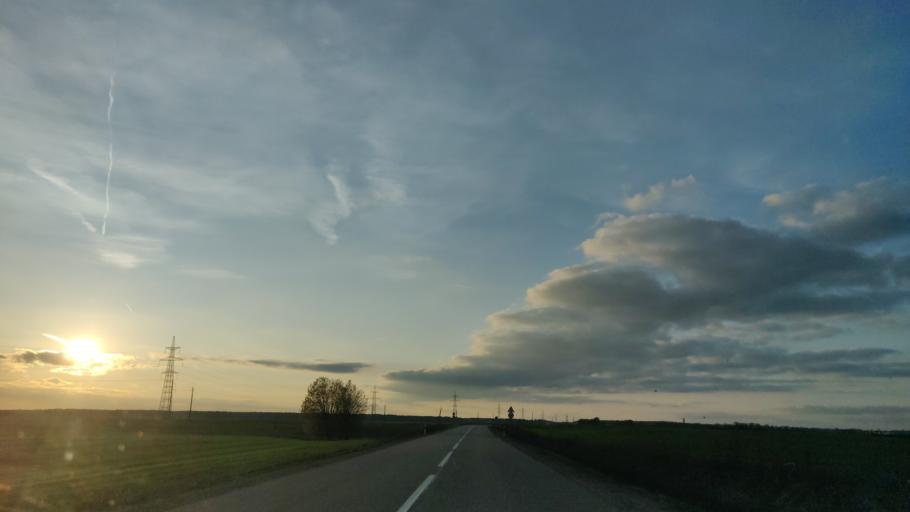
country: LT
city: Lentvaris
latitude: 54.6008
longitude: 25.0141
